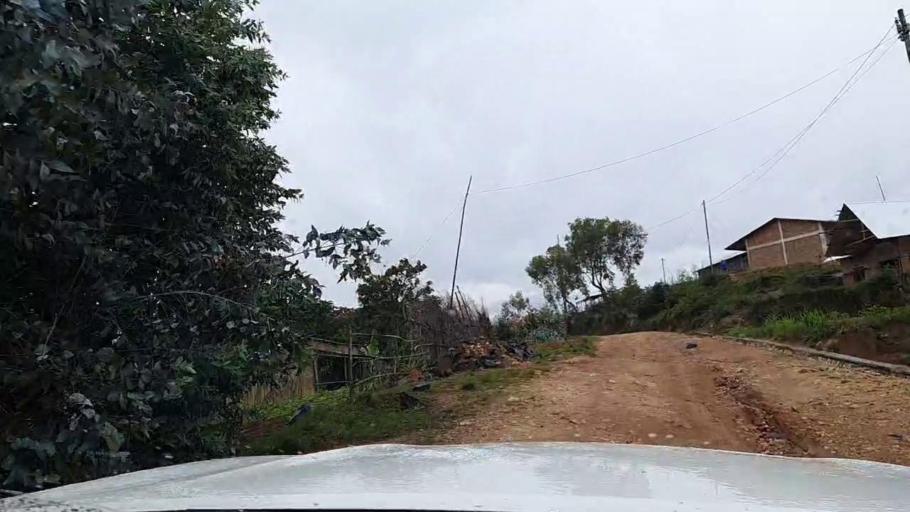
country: RW
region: Southern Province
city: Nzega
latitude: -2.4671
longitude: 29.4972
